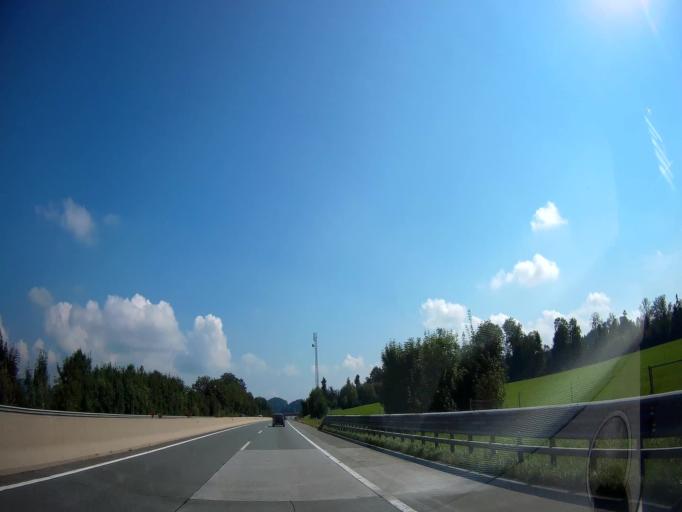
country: AT
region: Salzburg
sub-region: Politischer Bezirk Salzburg-Umgebung
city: Plainfeld
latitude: 47.8529
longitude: 13.1611
